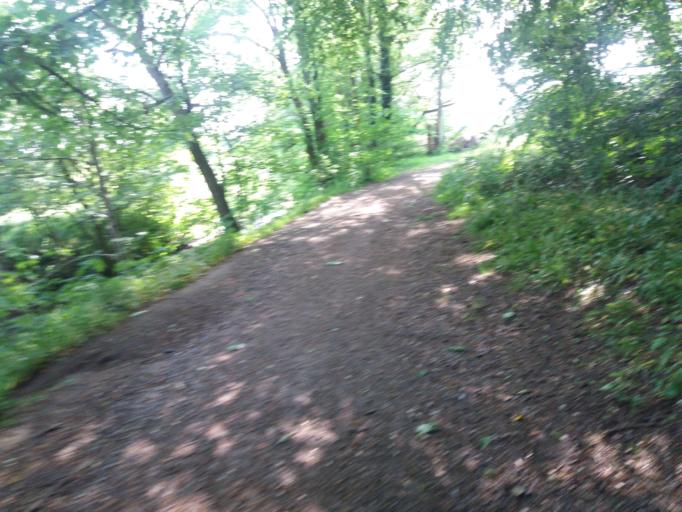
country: GB
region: England
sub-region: Lancashire
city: Coppull
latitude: 53.6496
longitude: -2.6582
